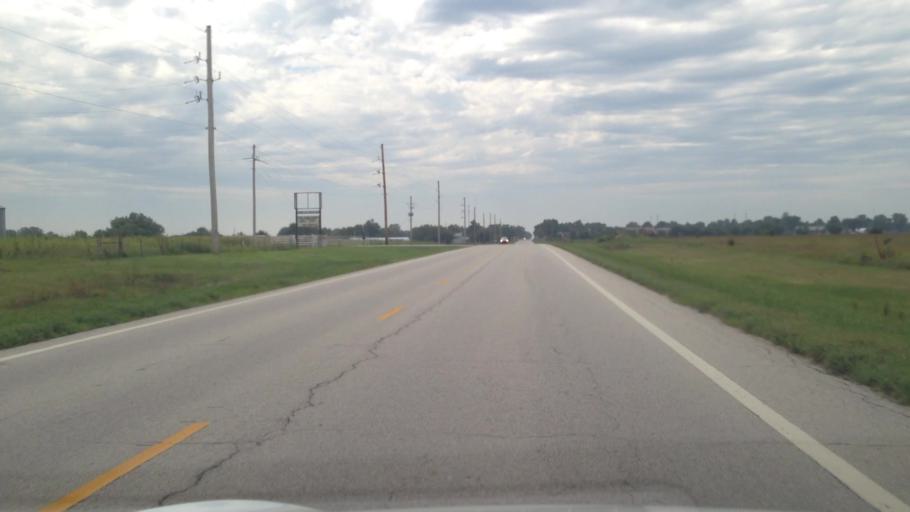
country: US
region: Kansas
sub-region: Allen County
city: Iola
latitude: 37.9293
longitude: -95.1701
